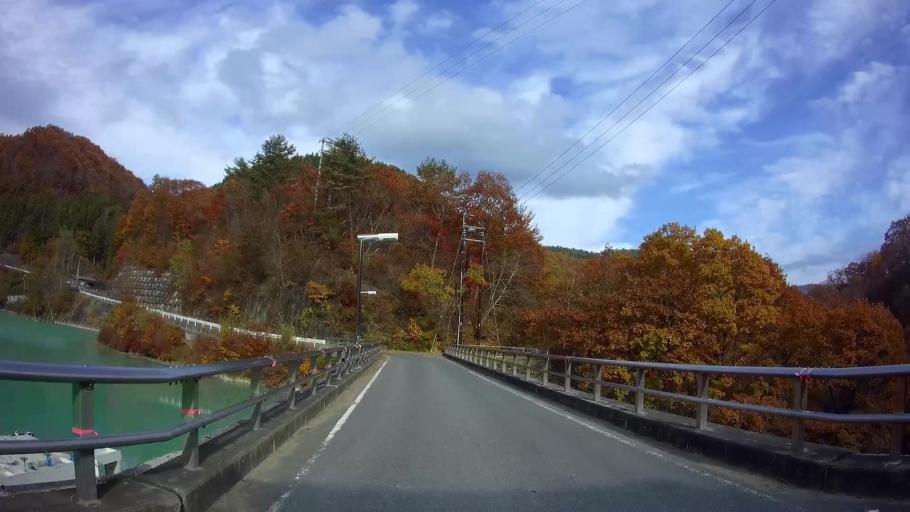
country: JP
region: Gunma
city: Nakanojomachi
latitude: 36.6282
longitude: 138.6341
